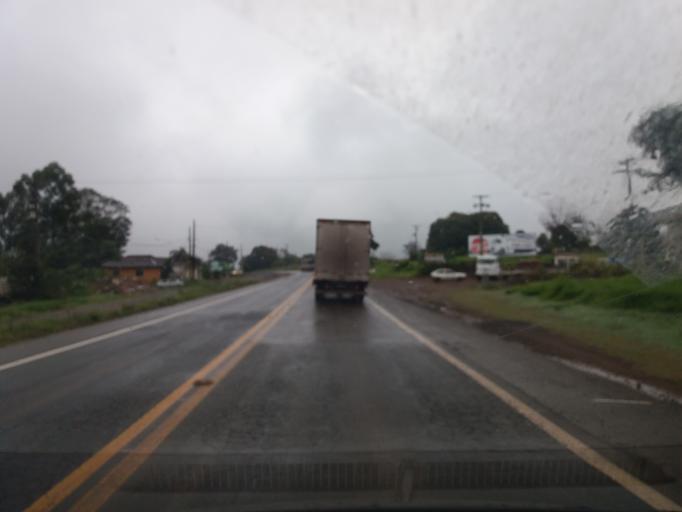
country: BR
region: Parana
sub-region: Realeza
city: Realeza
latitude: -25.4914
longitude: -53.5956
